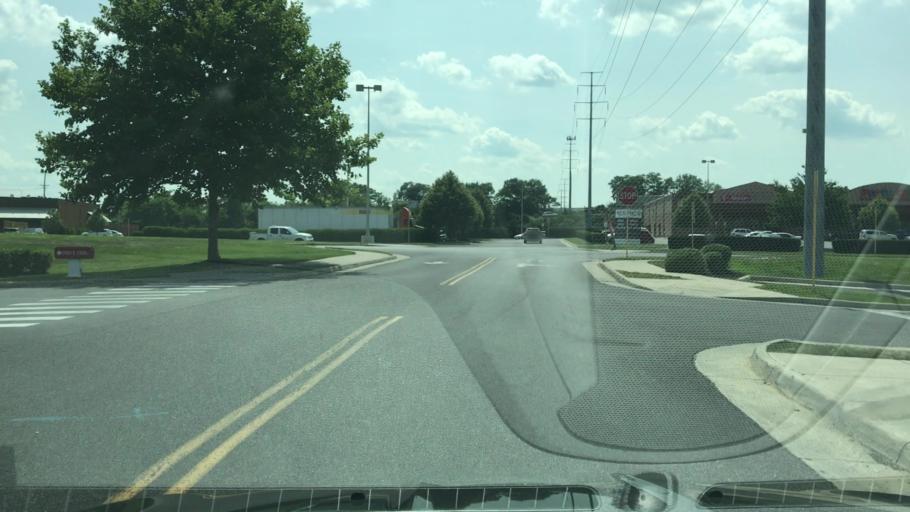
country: US
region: Virginia
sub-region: City of Winchester
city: Winchester
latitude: 39.2199
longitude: -78.1346
